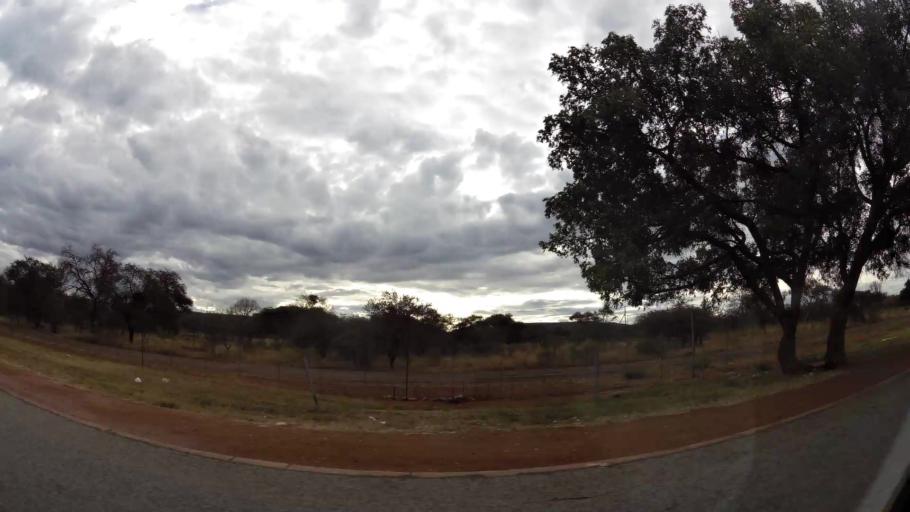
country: ZA
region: Limpopo
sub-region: Waterberg District Municipality
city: Modimolle
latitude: -24.5317
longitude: 28.7023
